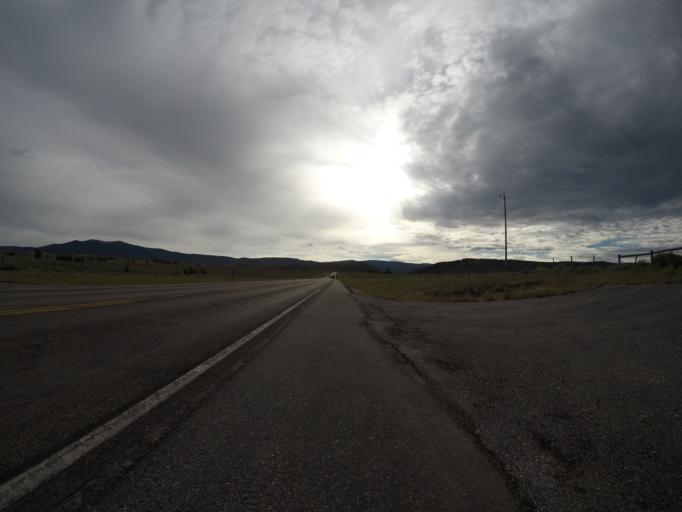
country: US
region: Wyoming
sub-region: Carbon County
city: Saratoga
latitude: 41.3569
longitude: -106.5975
